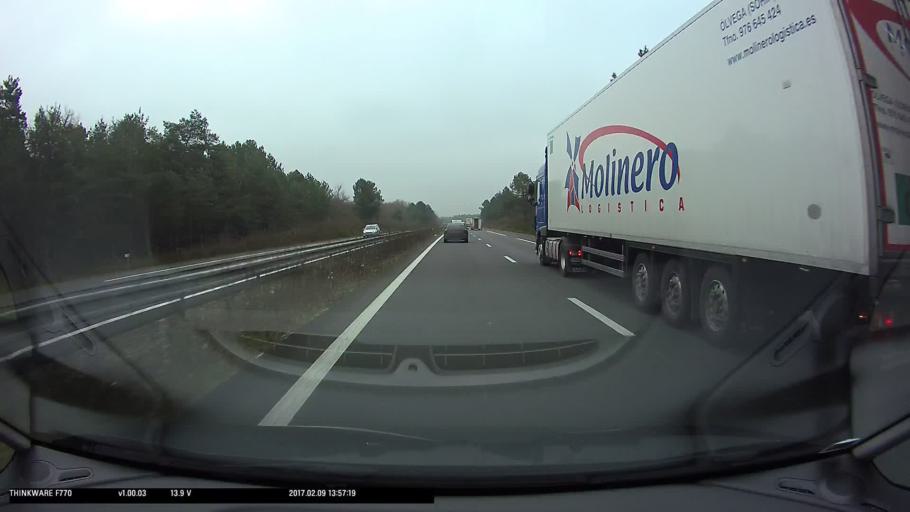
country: FR
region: Centre
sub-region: Departement du Loir-et-Cher
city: Chaumont-sur-Tharonne
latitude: 47.6227
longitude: 1.9608
